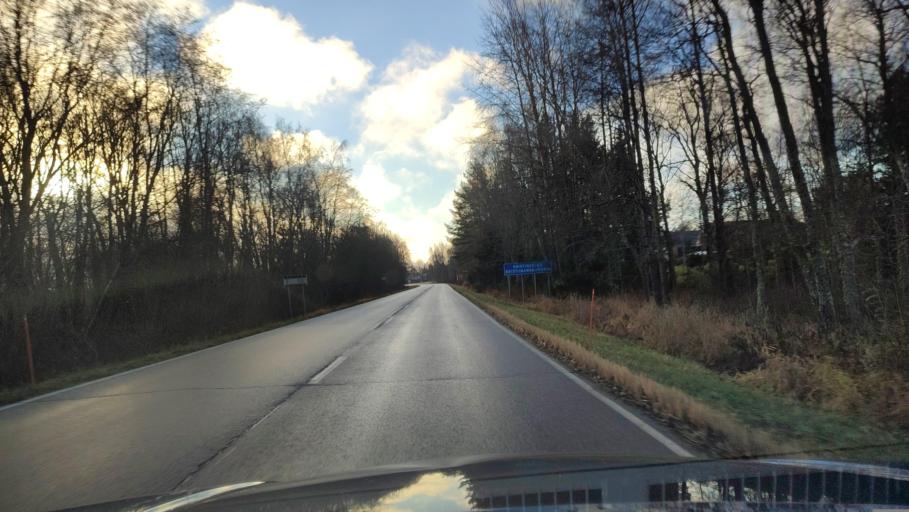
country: FI
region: Ostrobothnia
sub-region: Sydosterbotten
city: Kristinestad
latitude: 62.2845
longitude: 21.3781
